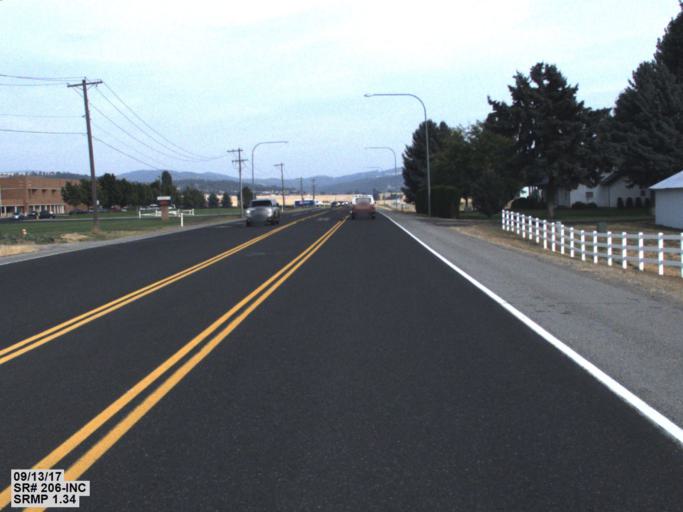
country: US
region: Washington
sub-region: Spokane County
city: Mead
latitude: 47.7874
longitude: -117.3262
